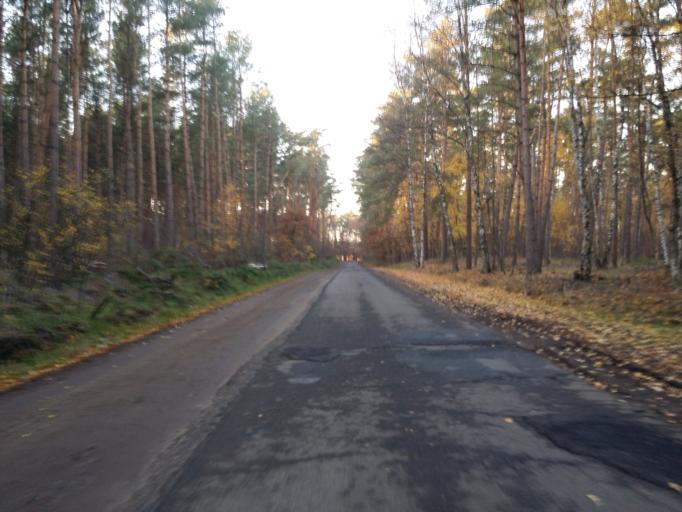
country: DE
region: Lower Saxony
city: Ahausen
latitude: 53.0810
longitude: 9.3045
